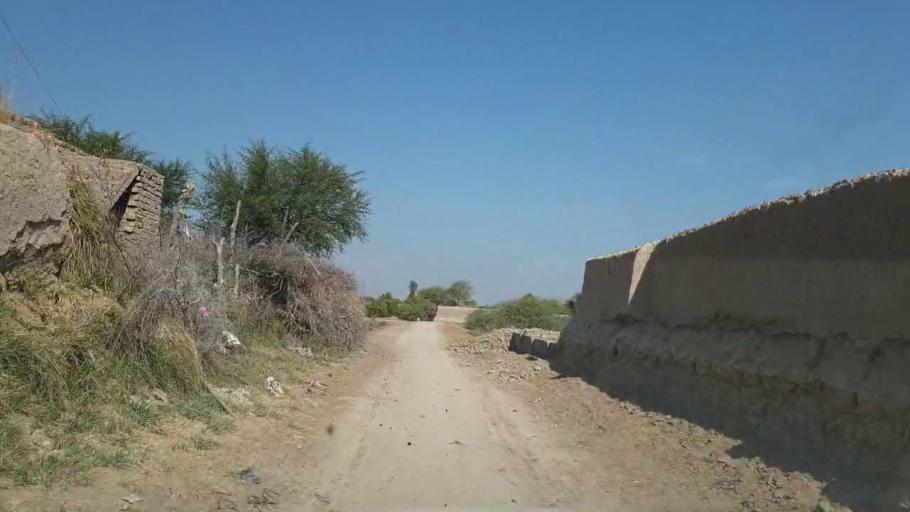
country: PK
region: Sindh
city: Mirpur Khas
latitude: 25.6304
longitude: 69.0954
